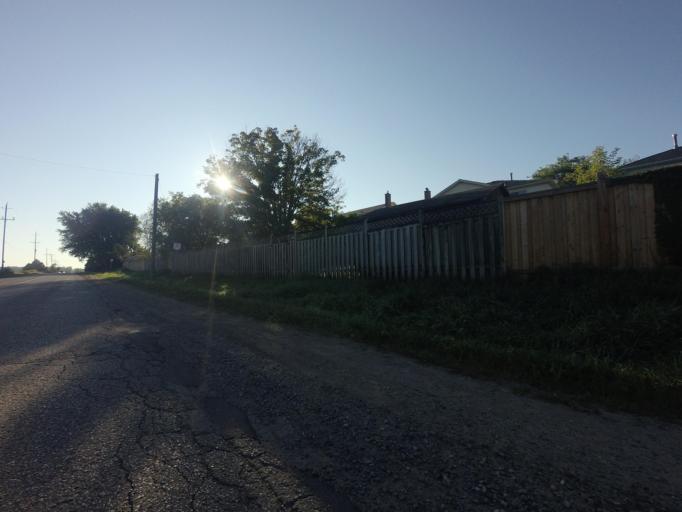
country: CA
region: Ontario
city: Bradford West Gwillimbury
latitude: 44.0349
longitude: -79.8067
